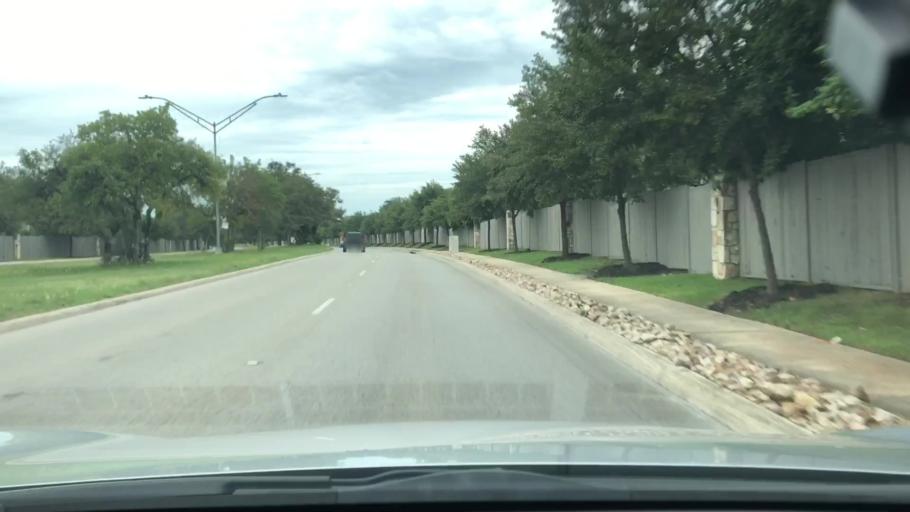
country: US
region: Texas
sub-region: Bexar County
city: Leon Valley
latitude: 29.4539
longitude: -98.6684
